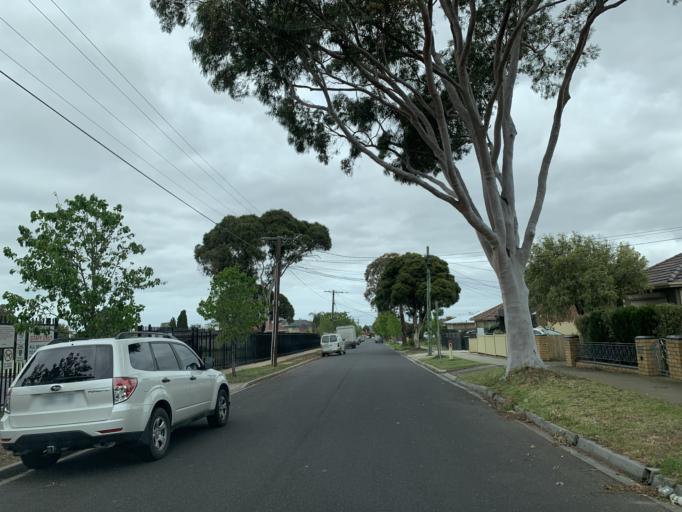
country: AU
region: Victoria
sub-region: Brimbank
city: St Albans
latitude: -37.7431
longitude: 144.8103
